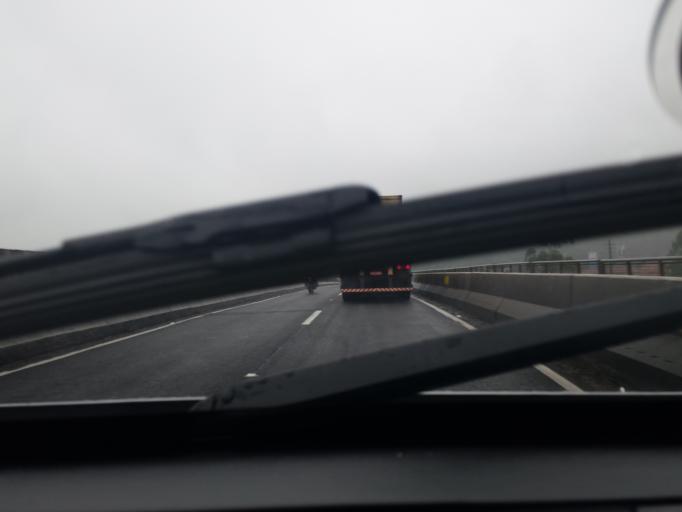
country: BR
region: Santa Catarina
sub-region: Navegantes
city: Navegantes
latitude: -26.8448
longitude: -48.7198
